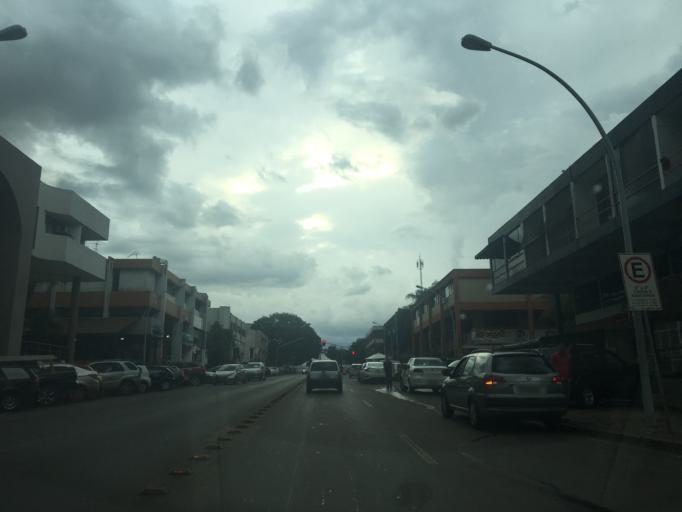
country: BR
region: Federal District
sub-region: Brasilia
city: Brasilia
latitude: -15.7400
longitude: -47.8929
